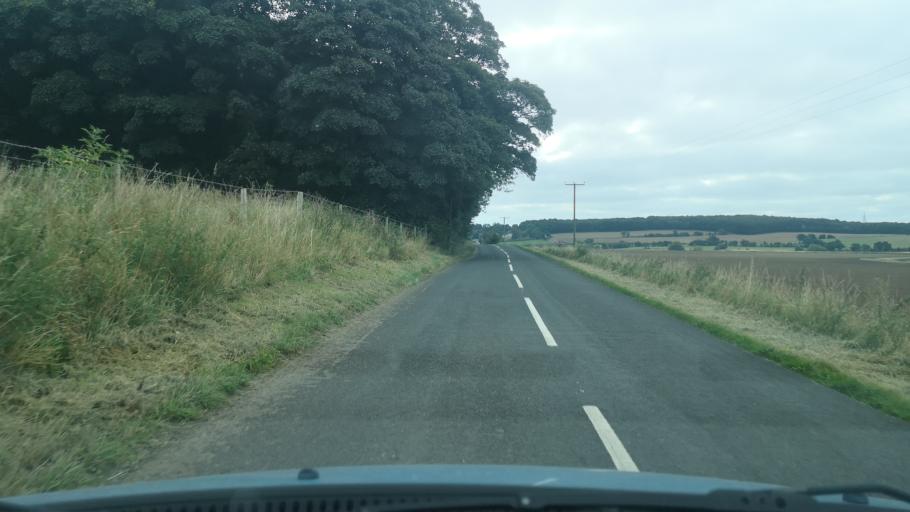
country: GB
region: England
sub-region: City and Borough of Wakefield
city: Darrington
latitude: 53.6569
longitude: -1.2773
